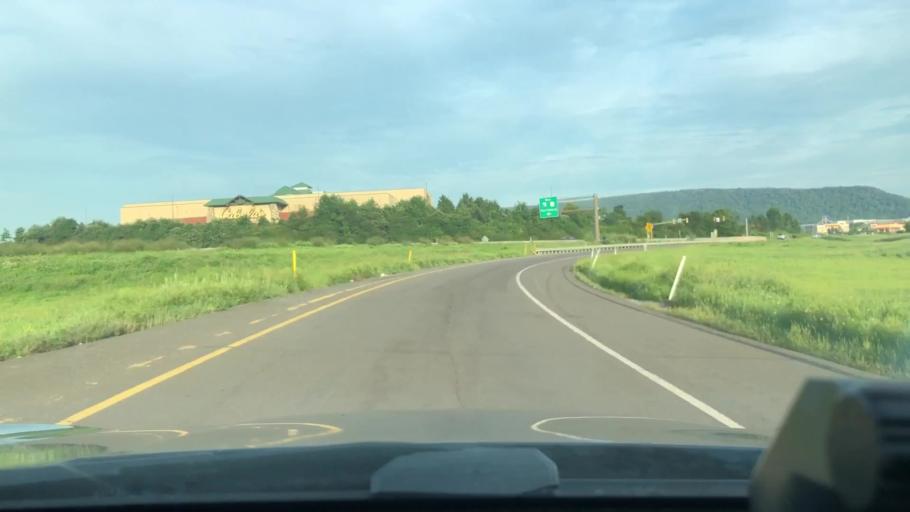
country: US
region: Pennsylvania
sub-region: Berks County
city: West Hamburg
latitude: 40.5577
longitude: -75.9976
